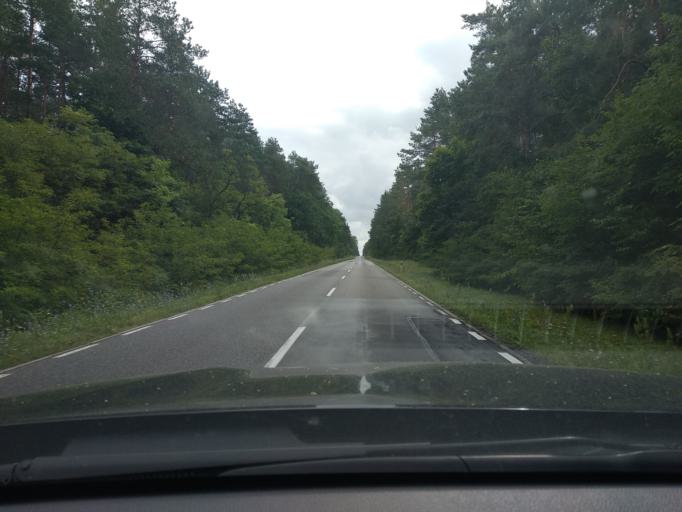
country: PL
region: Masovian Voivodeship
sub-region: Powiat pultuski
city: Obryte
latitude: 52.6444
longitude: 21.2615
